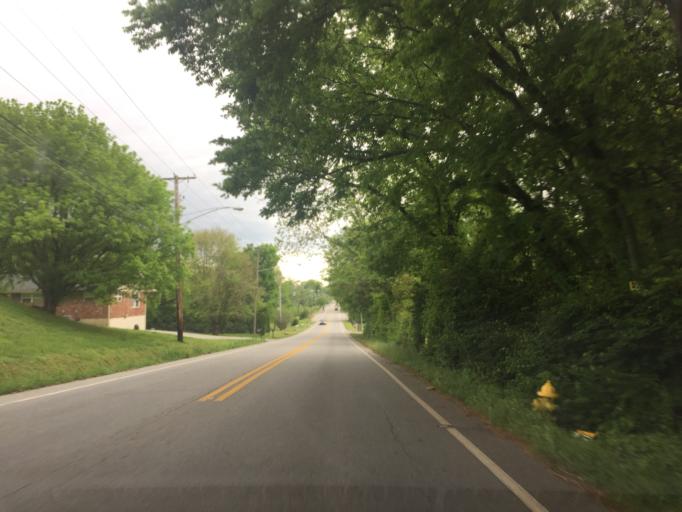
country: US
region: Tennessee
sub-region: Hamilton County
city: East Brainerd
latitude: 35.0542
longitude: -85.1621
